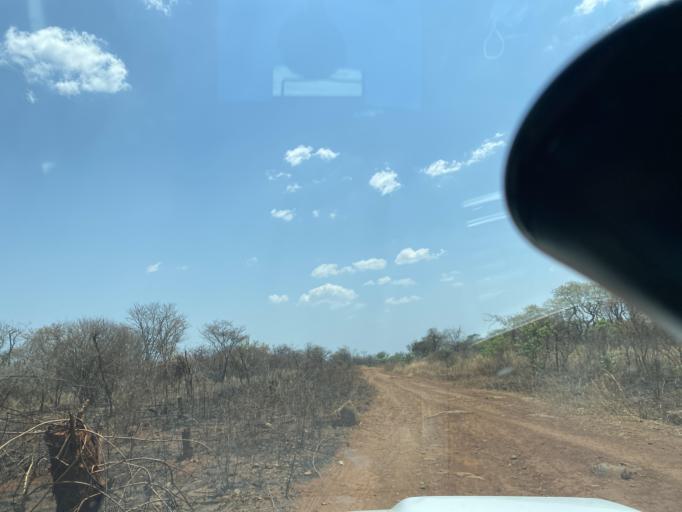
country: ZM
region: Lusaka
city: Lusaka
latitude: -15.5086
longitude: 28.0010
